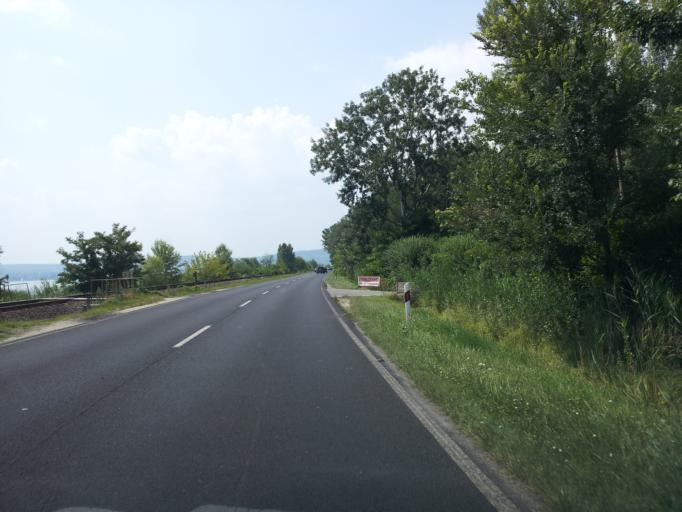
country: HU
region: Veszprem
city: Balatonkenese
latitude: 47.0395
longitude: 18.0727
